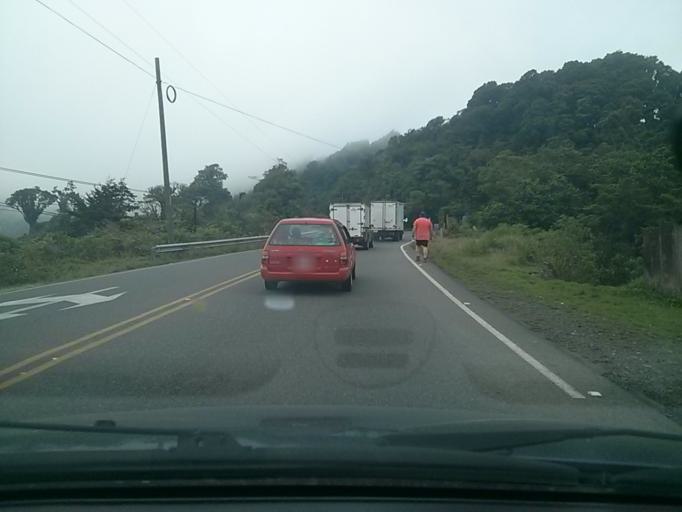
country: CR
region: Cartago
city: Tobosi
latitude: 9.7422
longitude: -83.9593
